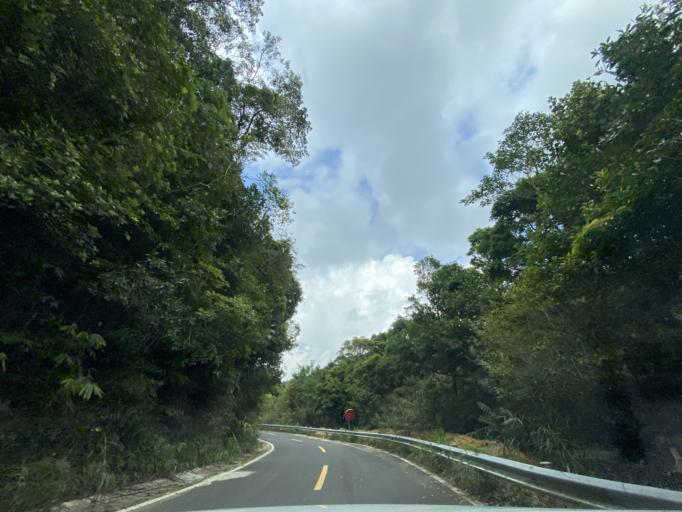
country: CN
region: Hainan
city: Benhao
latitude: 18.6991
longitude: 109.8831
